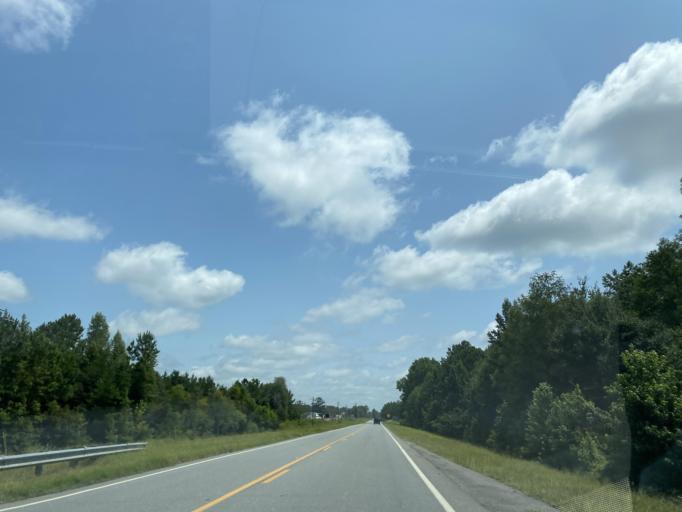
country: US
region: Georgia
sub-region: Telfair County
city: Helena
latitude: 32.0229
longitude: -83.0438
